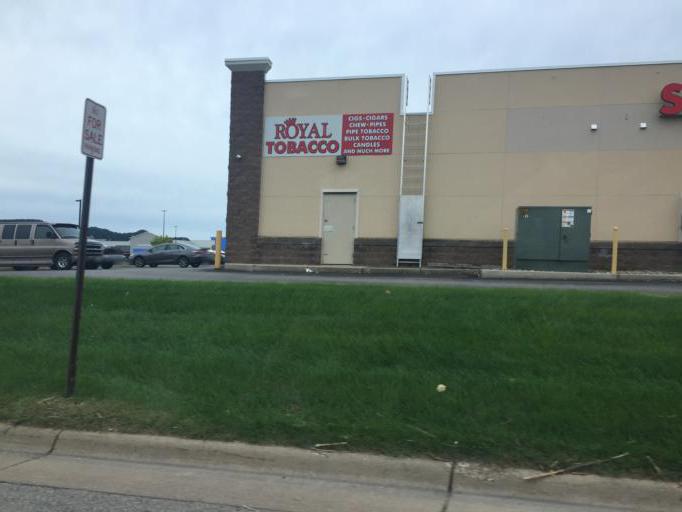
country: US
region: Minnesota
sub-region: Winona County
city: Winona
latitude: 44.0352
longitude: -91.6187
